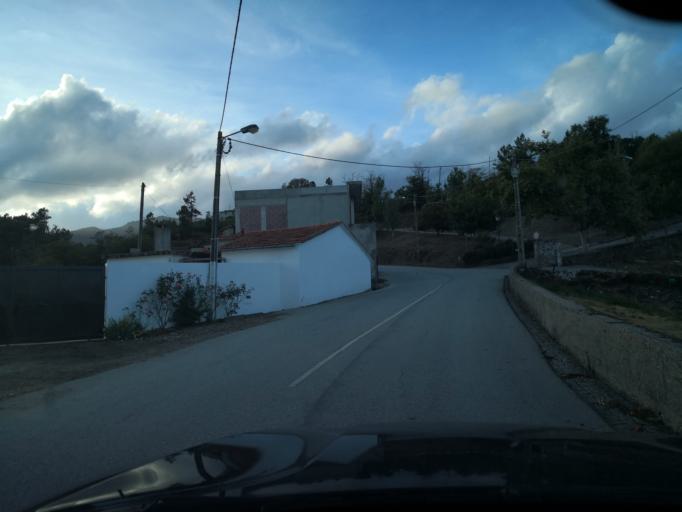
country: PT
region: Vila Real
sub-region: Santa Marta de Penaguiao
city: Santa Marta de Penaguiao
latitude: 41.2284
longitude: -7.8320
